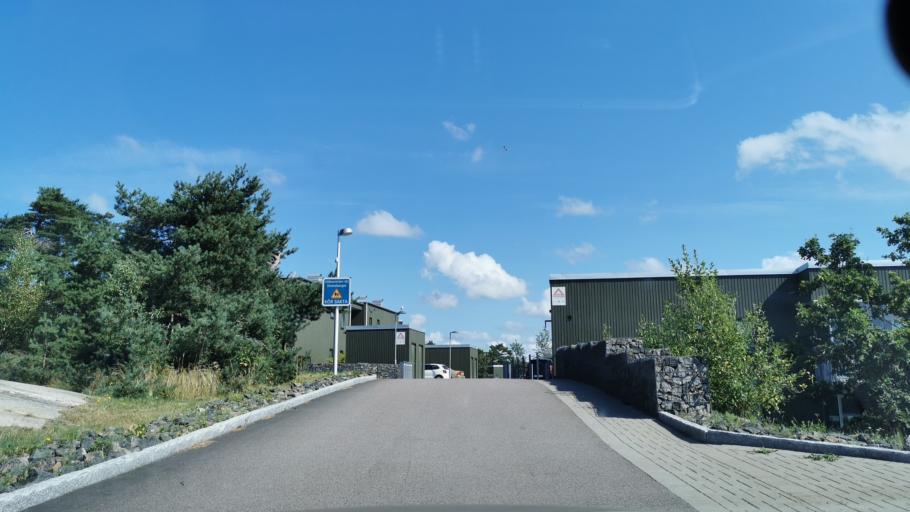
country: SE
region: Vaestra Goetaland
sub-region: Goteborg
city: Majorna
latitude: 57.6557
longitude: 11.9105
